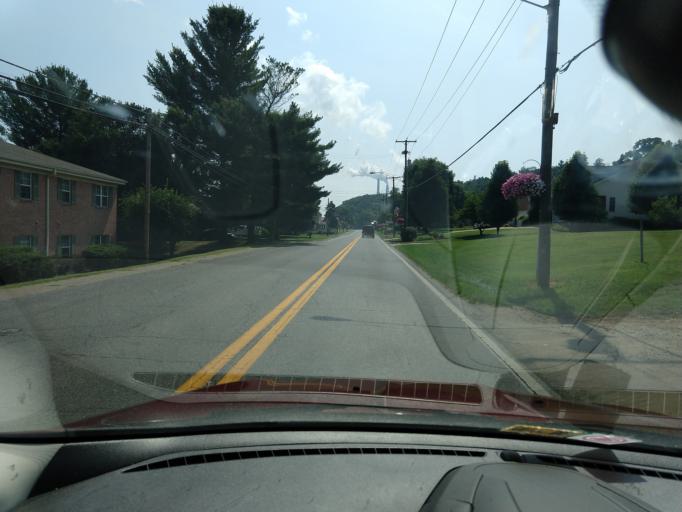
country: US
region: West Virginia
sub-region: Mason County
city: New Haven
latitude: 38.9858
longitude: -81.9691
